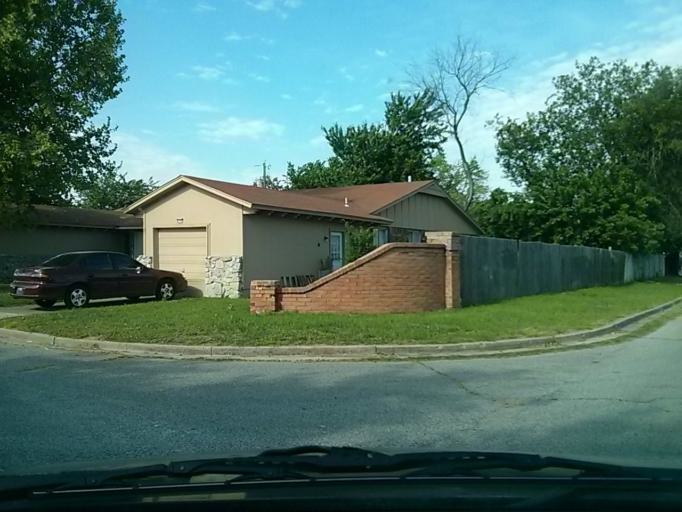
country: US
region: Oklahoma
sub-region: Tulsa County
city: Jenks
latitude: 36.0723
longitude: -95.9768
